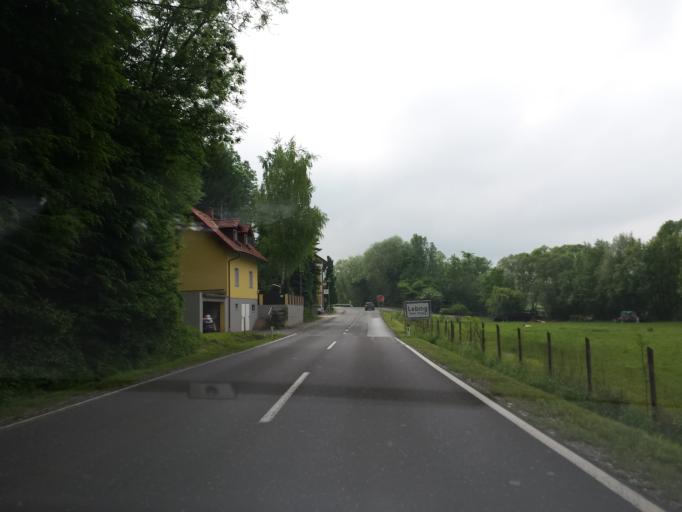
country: AT
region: Styria
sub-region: Politischer Bezirk Weiz
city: Floing
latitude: 47.2526
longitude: 15.7253
